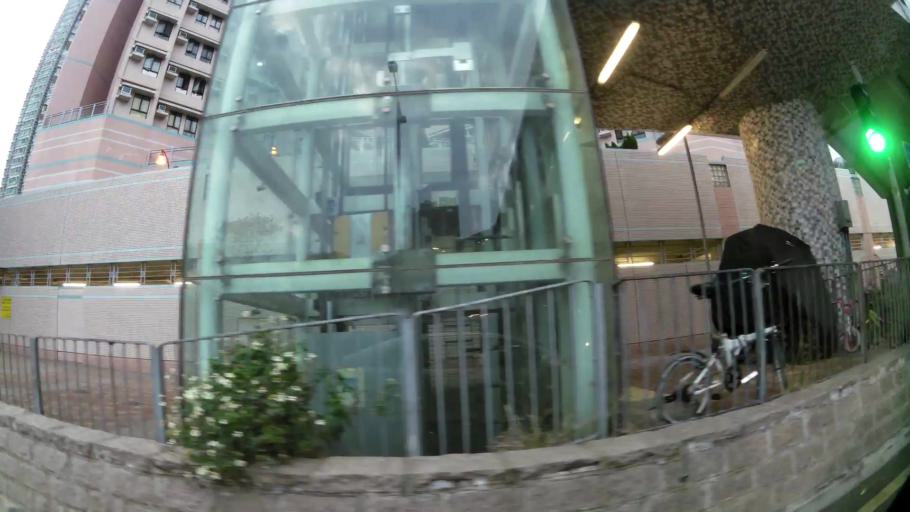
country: HK
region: Sham Shui Po
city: Sham Shui Po
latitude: 22.3234
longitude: 114.1593
